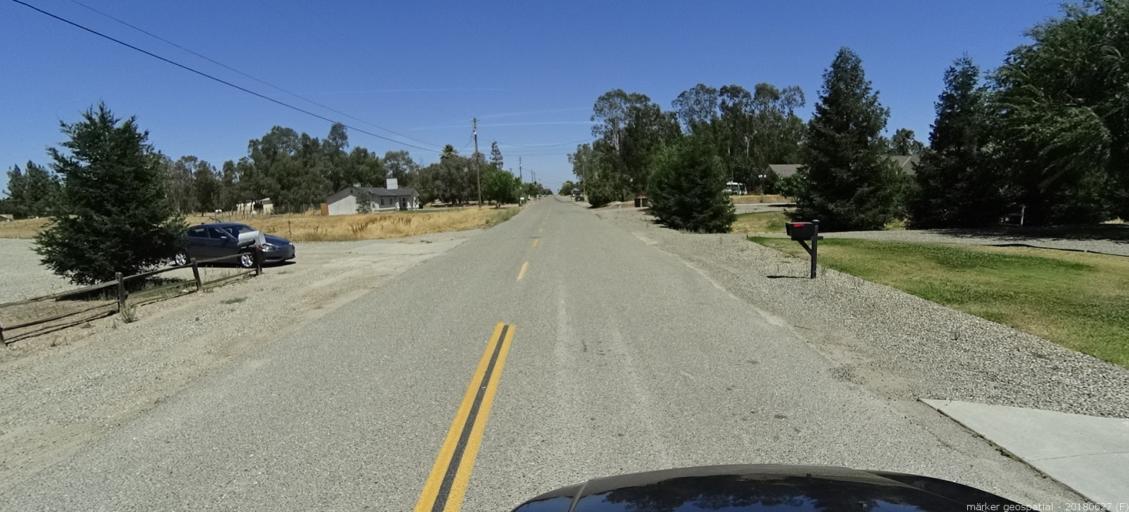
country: US
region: California
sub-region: Madera County
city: Bonadelle Ranchos-Madera Ranchos
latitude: 36.9617
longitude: -119.9181
